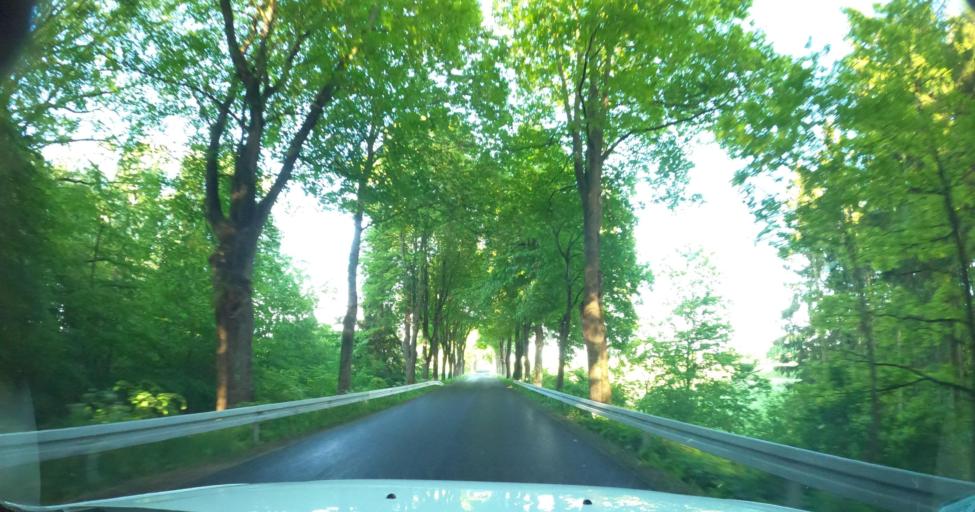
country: PL
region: Warmian-Masurian Voivodeship
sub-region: Powiat braniewski
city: Braniewo
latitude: 54.2825
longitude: 19.8591
